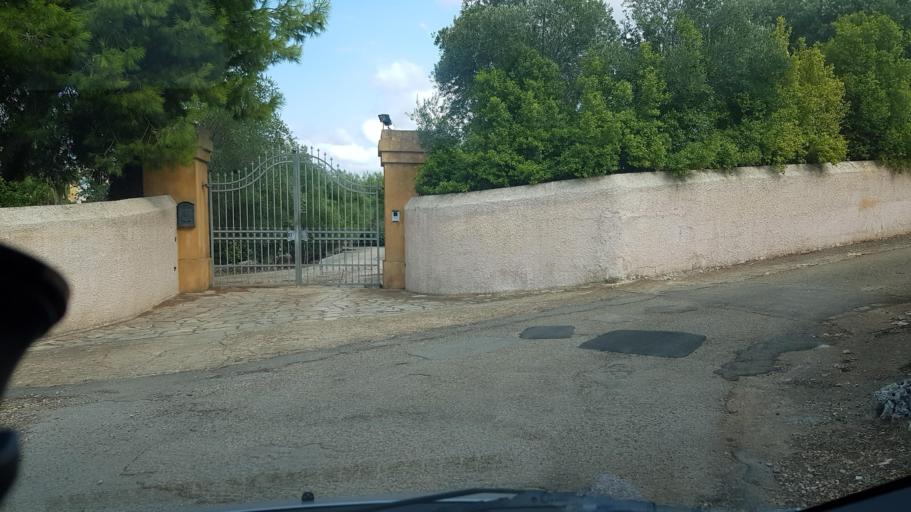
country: IT
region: Apulia
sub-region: Provincia di Brindisi
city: San Vito dei Normanni
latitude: 40.6674
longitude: 17.7212
